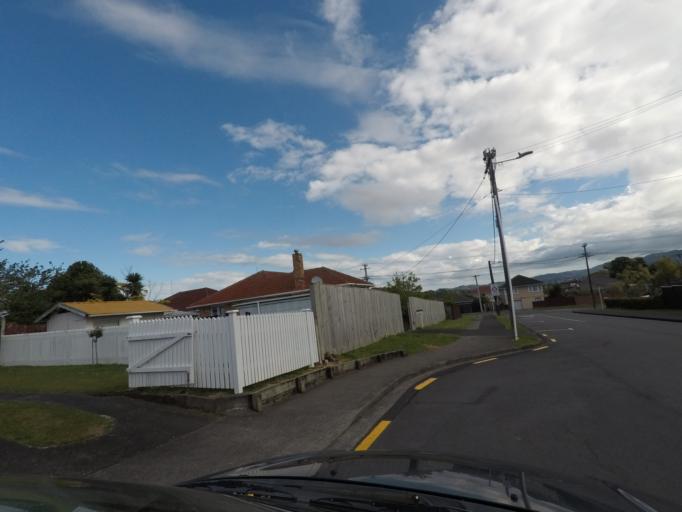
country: NZ
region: Auckland
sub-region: Auckland
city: Rosebank
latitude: -36.8690
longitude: 174.6451
